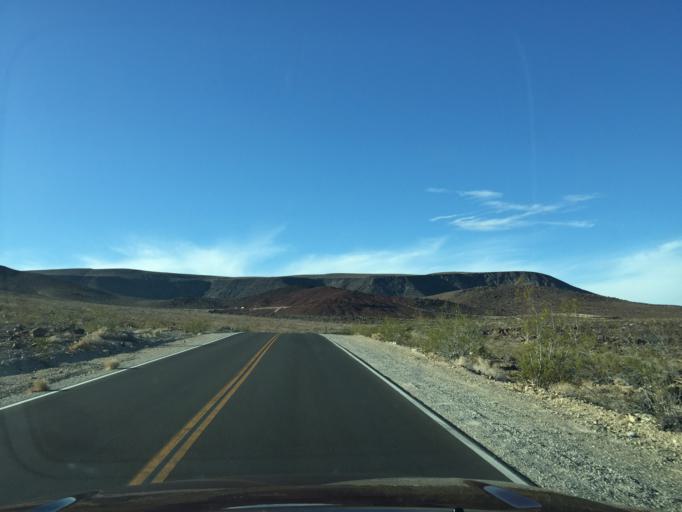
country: US
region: California
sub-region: Inyo County
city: Lone Pine
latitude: 36.3527
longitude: -117.5283
